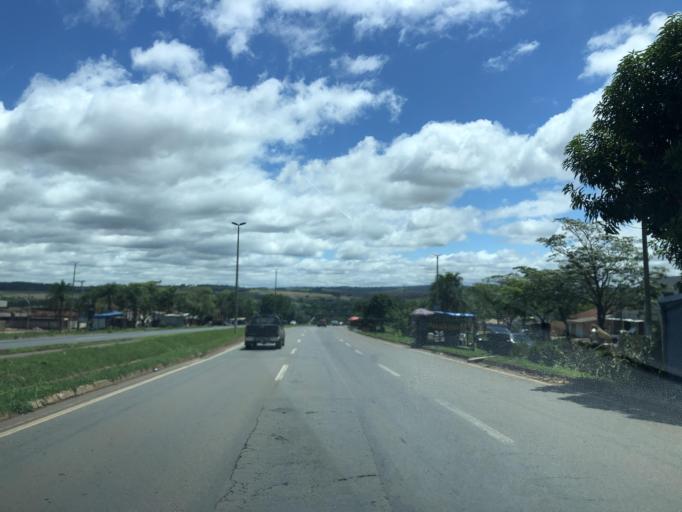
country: BR
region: Goias
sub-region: Goianapolis
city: Goianapolis
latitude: -16.4874
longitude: -49.0953
